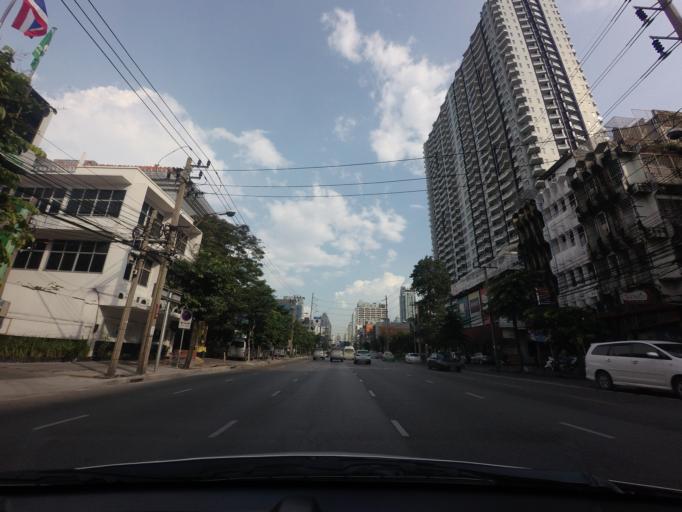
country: TH
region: Bangkok
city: Ratchathewi
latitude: 13.7555
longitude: 100.5254
